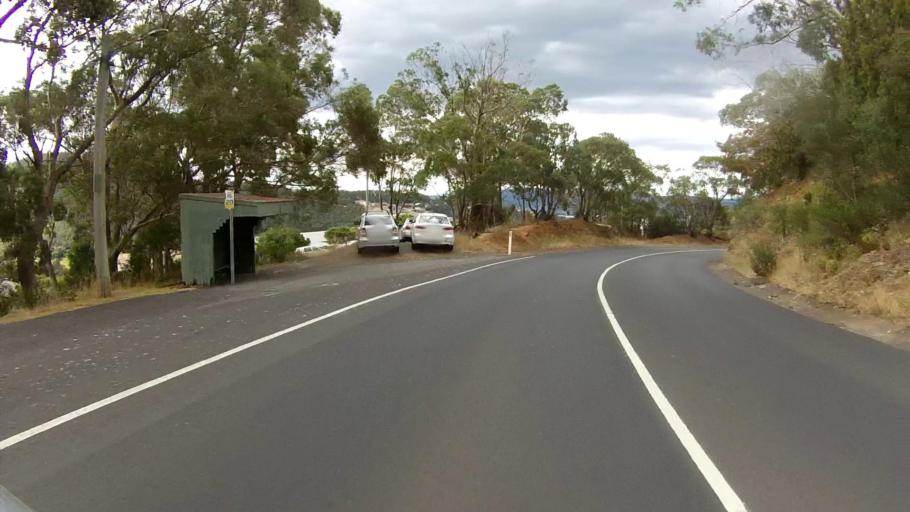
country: AU
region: Tasmania
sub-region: Hobart
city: Dynnyrne
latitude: -42.9007
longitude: 147.2960
